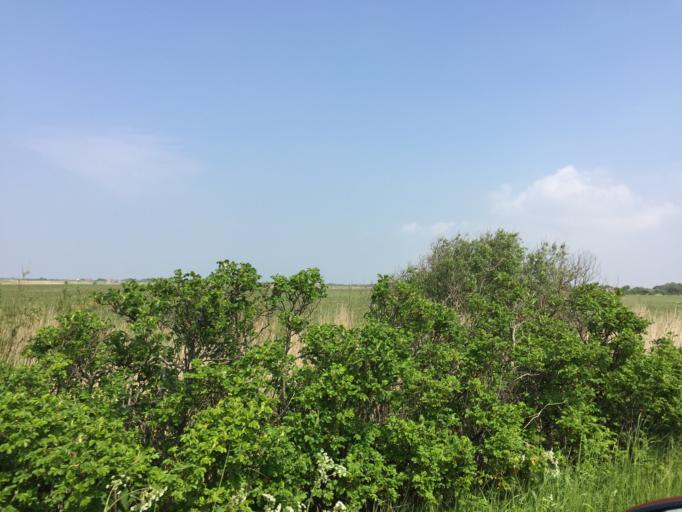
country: DK
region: South Denmark
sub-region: Esbjerg Kommune
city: Tjaereborg
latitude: 55.2675
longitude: 8.5532
